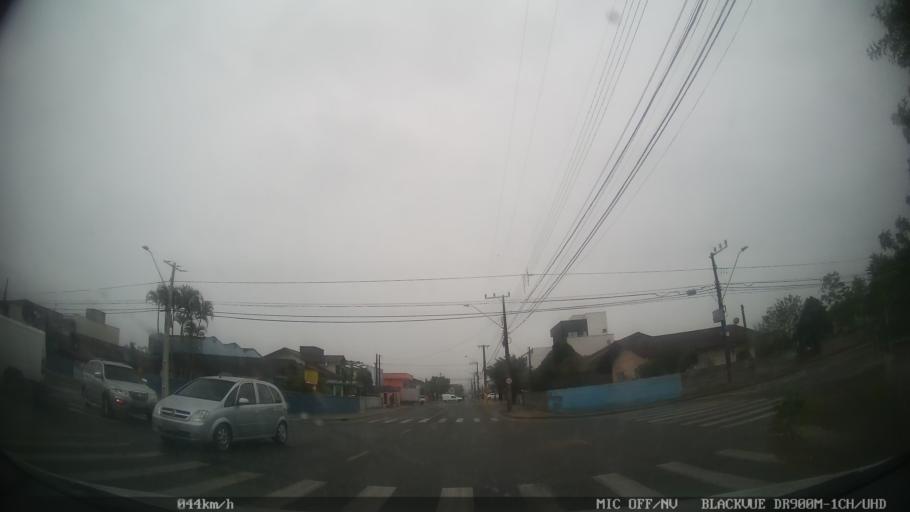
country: BR
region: Santa Catarina
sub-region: Joinville
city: Joinville
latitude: -26.2674
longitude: -48.7994
